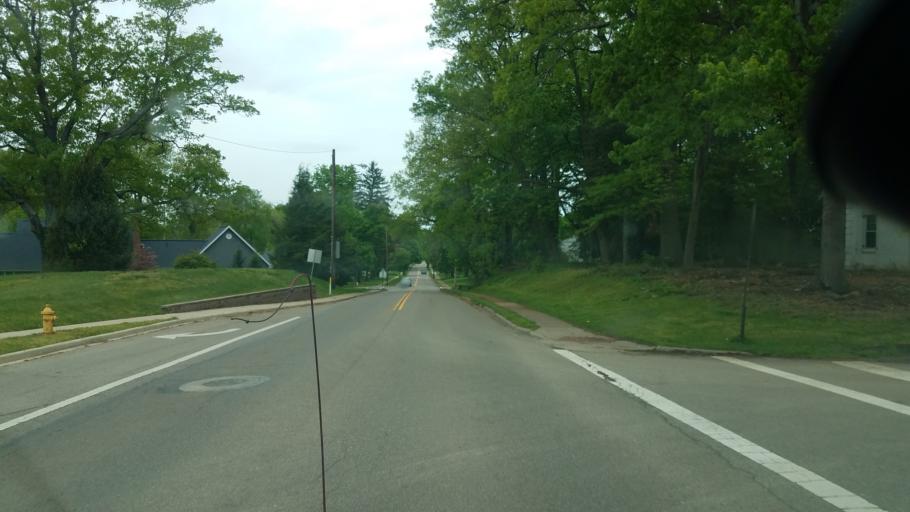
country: US
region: Ohio
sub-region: Coshocton County
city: Coshocton
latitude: 40.2604
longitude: -81.8442
